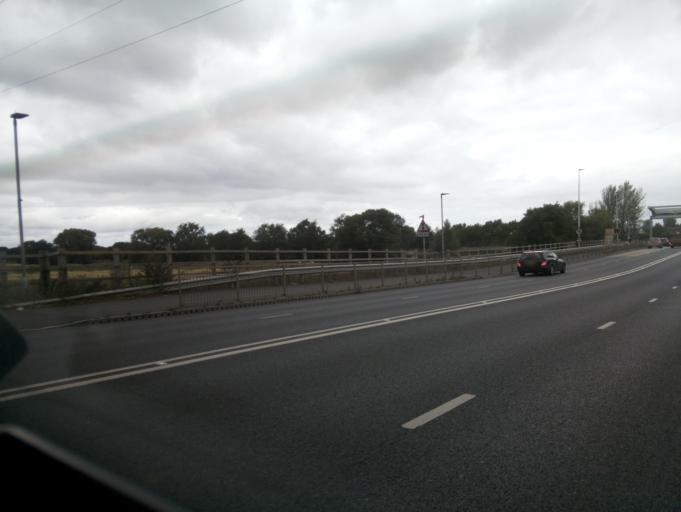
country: GB
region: England
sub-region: Devon
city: Exminster
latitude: 50.6934
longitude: -3.5027
